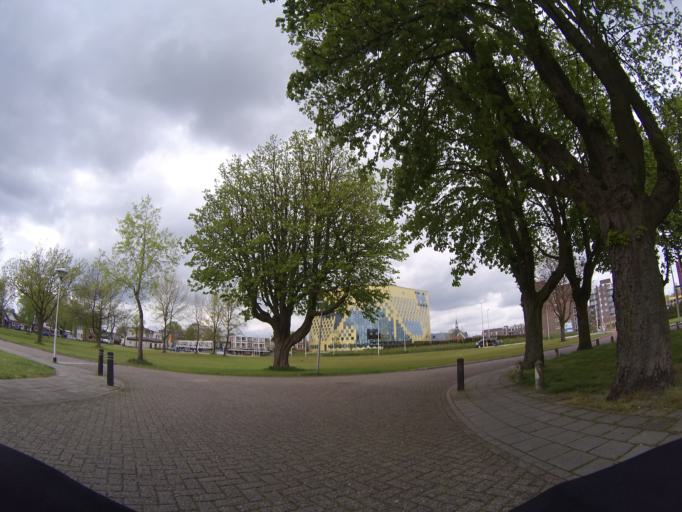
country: NL
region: Overijssel
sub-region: Gemeente Hardenberg
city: Hardenberg
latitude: 52.5727
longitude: 6.6203
